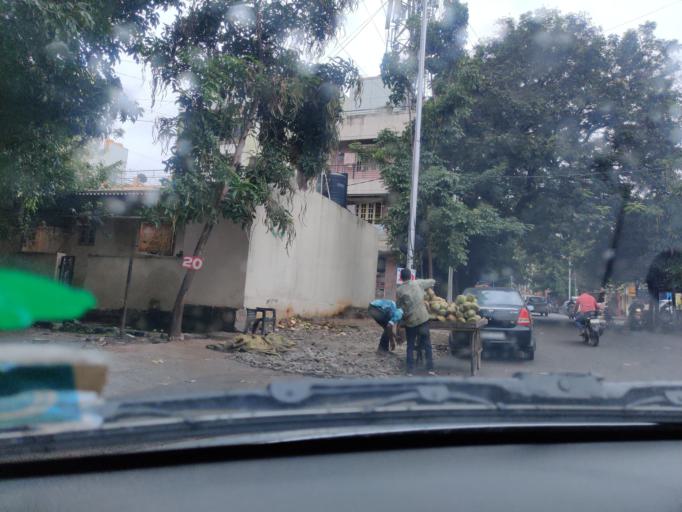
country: IN
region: Karnataka
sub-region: Bangalore Urban
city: Bangalore
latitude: 13.0172
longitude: 77.6394
